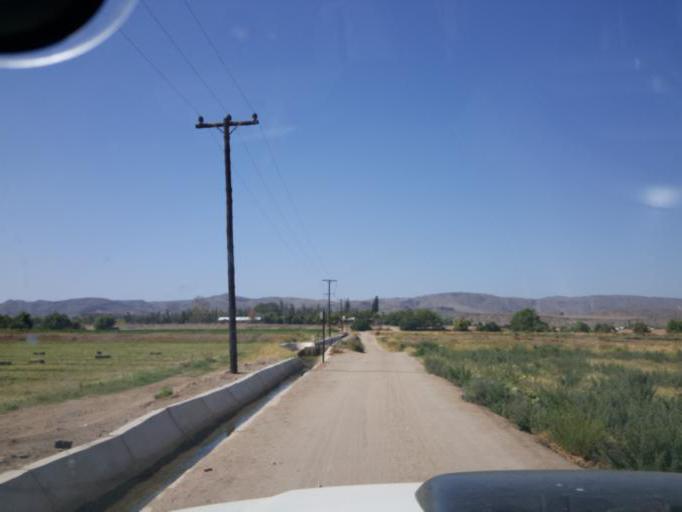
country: ZA
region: Northern Cape
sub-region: Namakwa District Municipality
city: Port Nolloth
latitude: -28.6919
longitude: 17.5848
